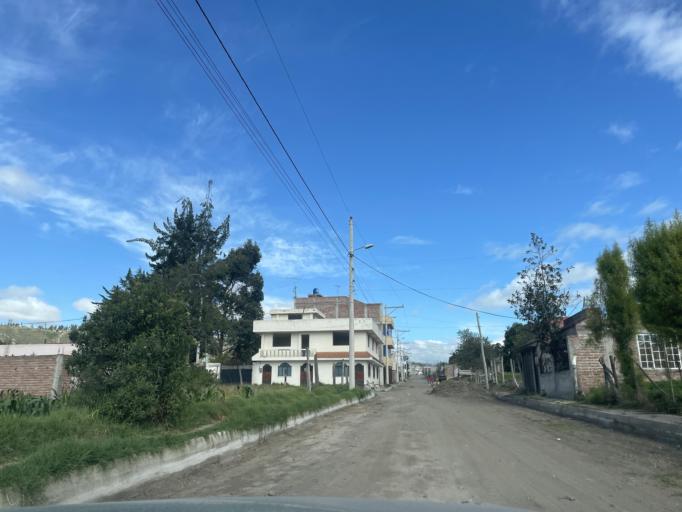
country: EC
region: Chimborazo
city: Guano
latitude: -1.6060
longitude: -78.6258
